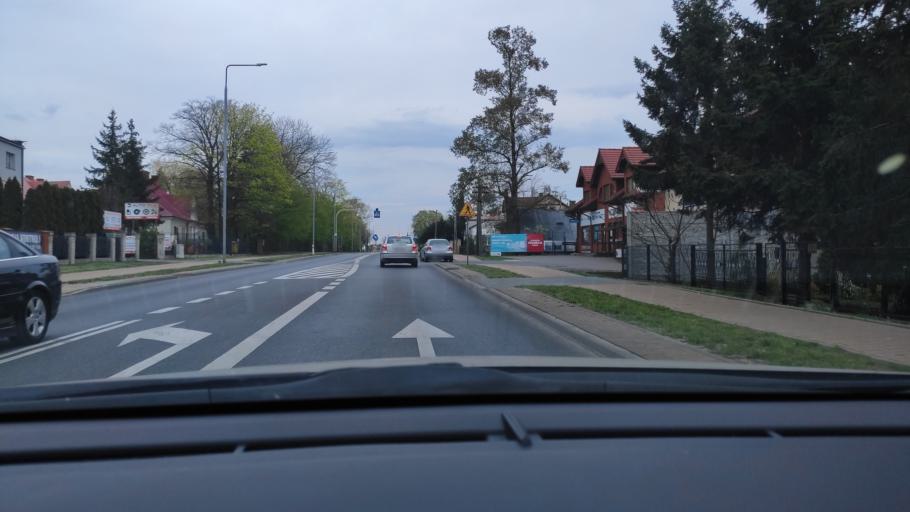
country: PL
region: Masovian Voivodeship
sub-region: Powiat zwolenski
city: Zwolen
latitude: 51.3584
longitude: 21.5690
